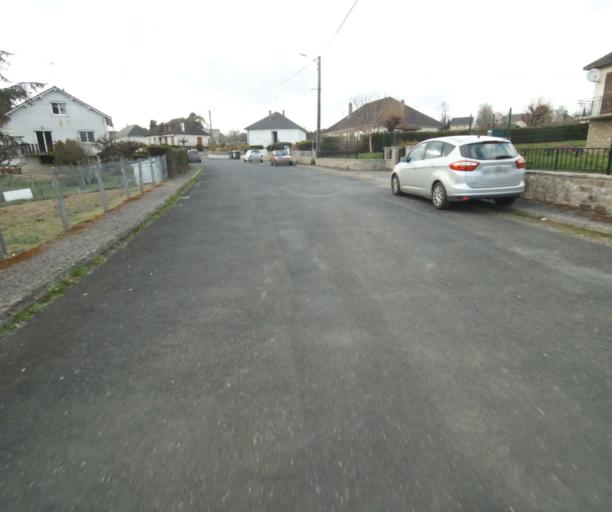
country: FR
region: Limousin
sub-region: Departement de la Correze
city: Saint-Clement
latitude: 45.3525
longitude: 1.6424
